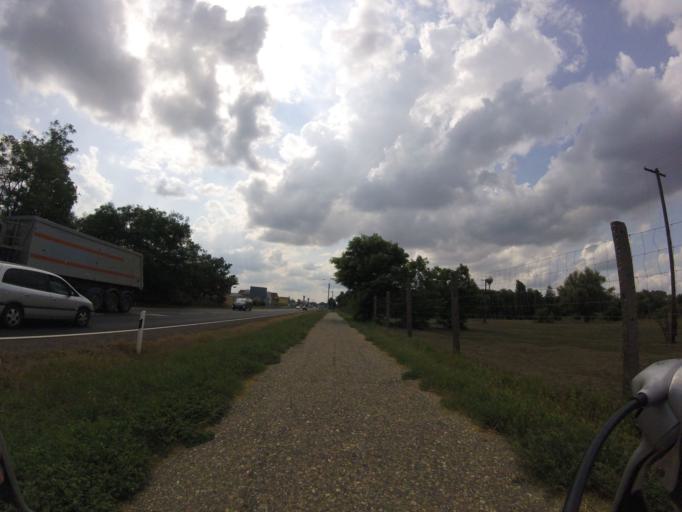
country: HU
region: Szabolcs-Szatmar-Bereg
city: Nyiregyhaza
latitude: 47.9710
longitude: 21.7455
